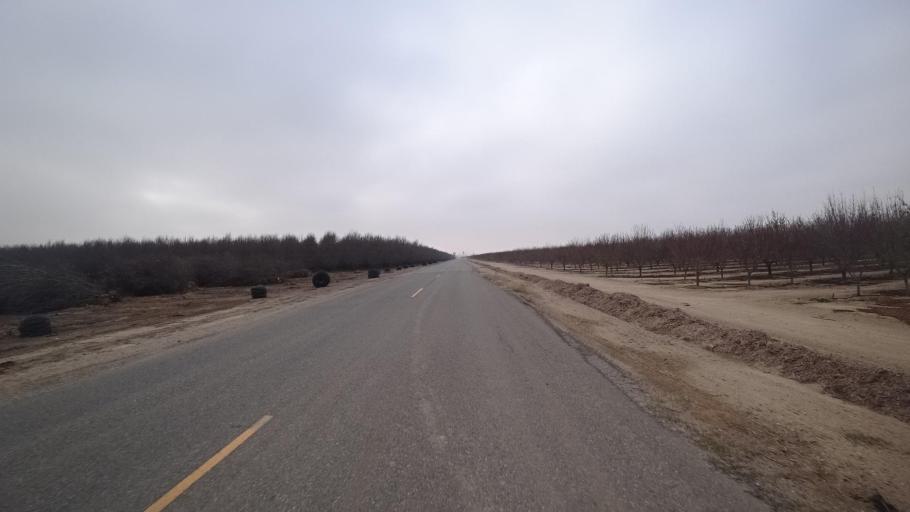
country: US
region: California
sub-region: Kern County
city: Maricopa
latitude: 35.1231
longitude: -119.3503
